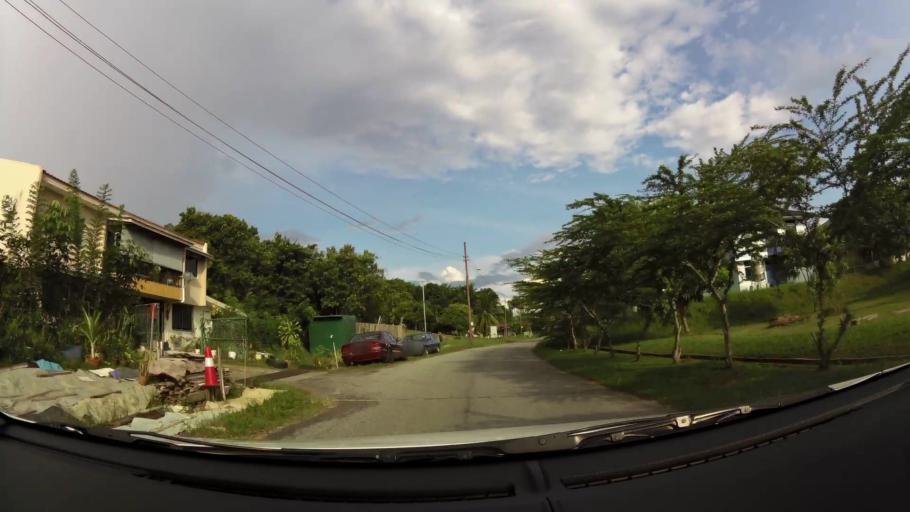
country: BN
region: Brunei and Muara
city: Bandar Seri Begawan
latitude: 4.9690
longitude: 114.9804
